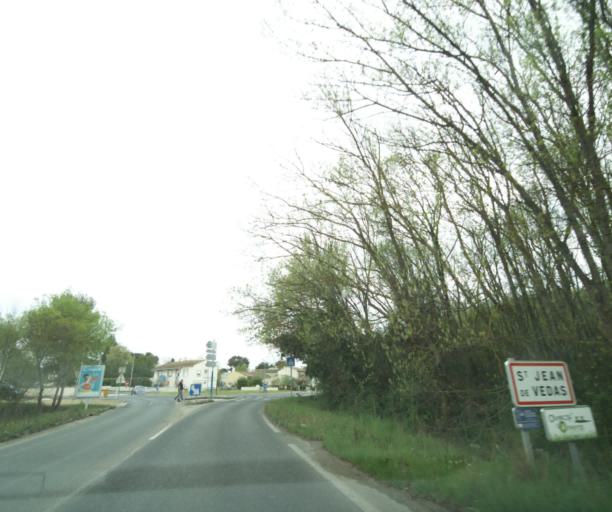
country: FR
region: Languedoc-Roussillon
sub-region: Departement de l'Herault
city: Saint-Jean-de-Vedas
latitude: 43.5832
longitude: 3.8194
